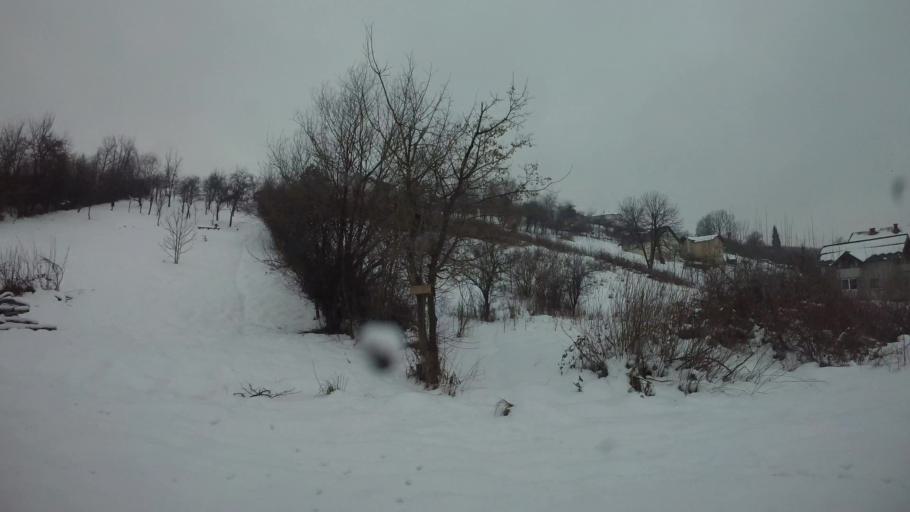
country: BA
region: Federation of Bosnia and Herzegovina
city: Hadzici
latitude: 43.8506
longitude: 18.2774
